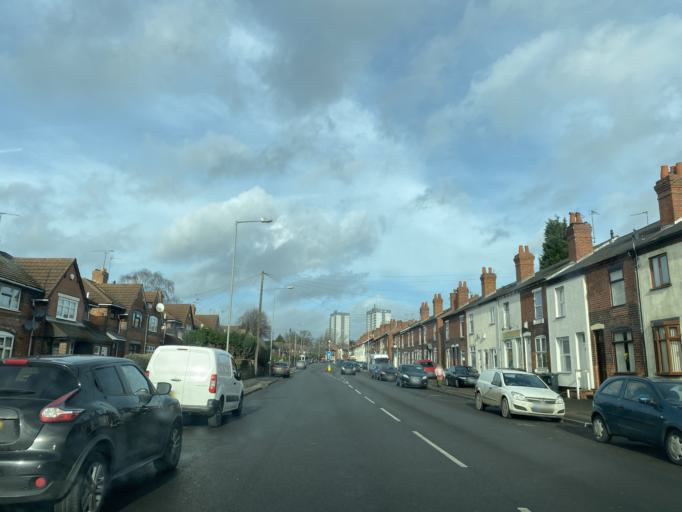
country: GB
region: England
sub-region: Walsall
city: Walsall
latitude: 52.5699
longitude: -1.9805
